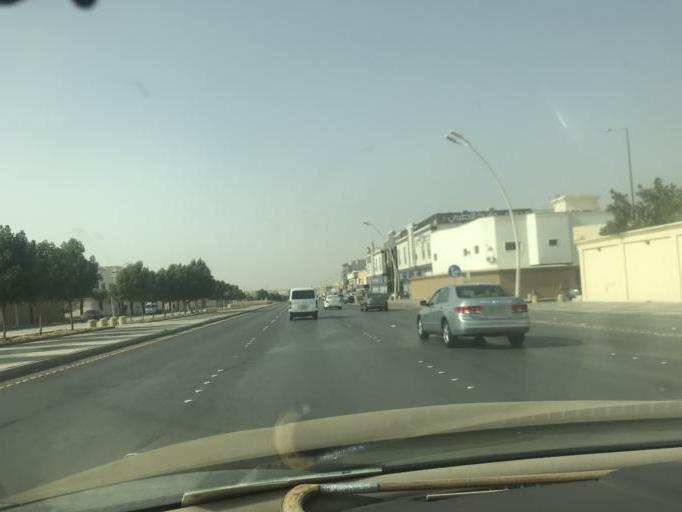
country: SA
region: Ar Riyad
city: Riyadh
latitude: 24.6737
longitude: 46.8031
